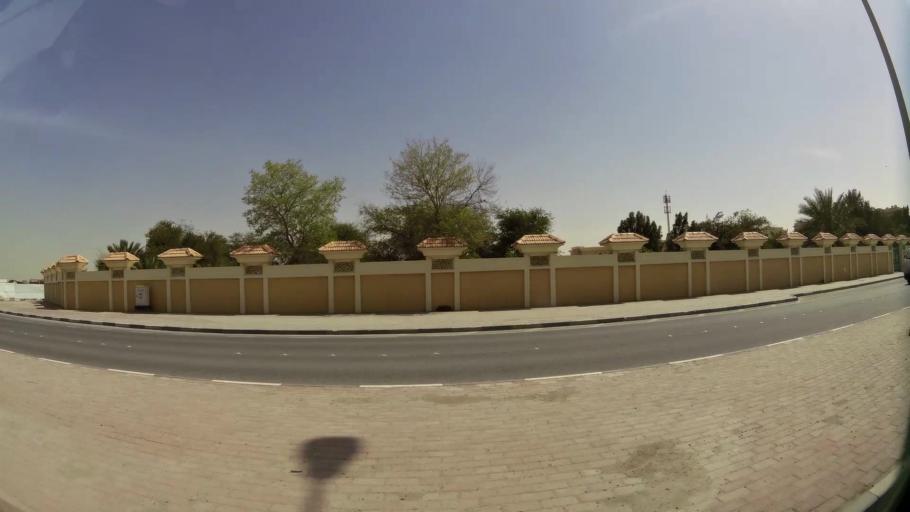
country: QA
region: Baladiyat ar Rayyan
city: Ar Rayyan
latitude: 25.2663
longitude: 51.4131
